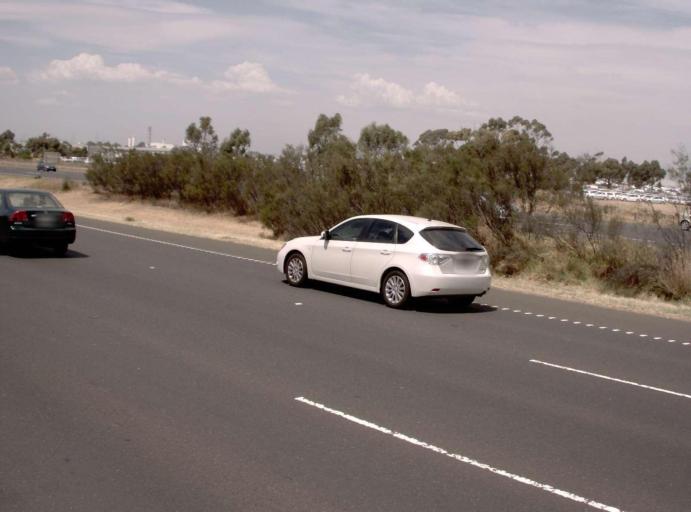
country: AU
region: Victoria
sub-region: Hobsons Bay
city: Laverton
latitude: -37.8372
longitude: 144.8003
